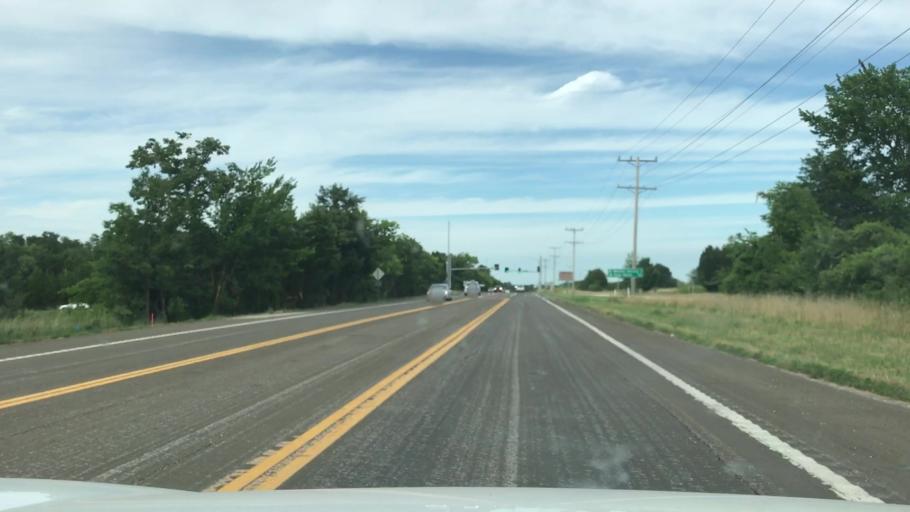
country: US
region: Missouri
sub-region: Saint Charles County
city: Weldon Spring
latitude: 38.7022
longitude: -90.7114
